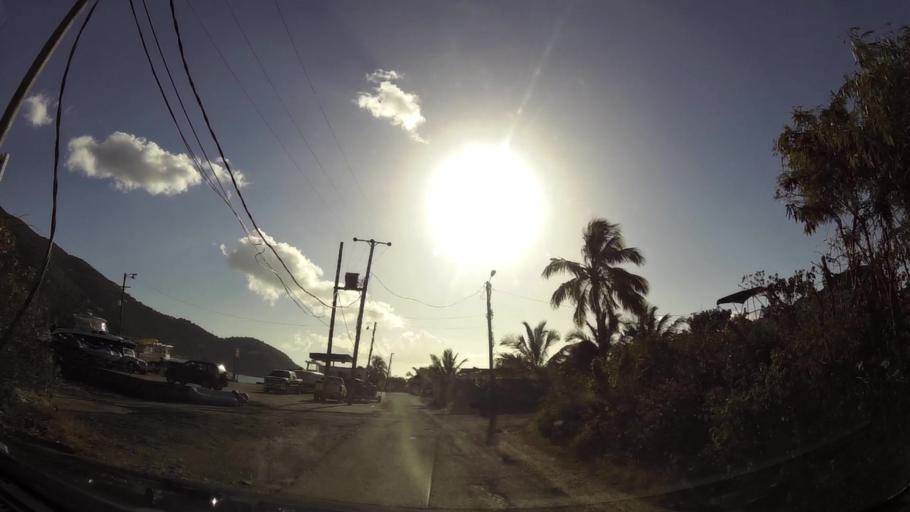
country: VG
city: Road Town
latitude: 18.4302
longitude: -64.6607
